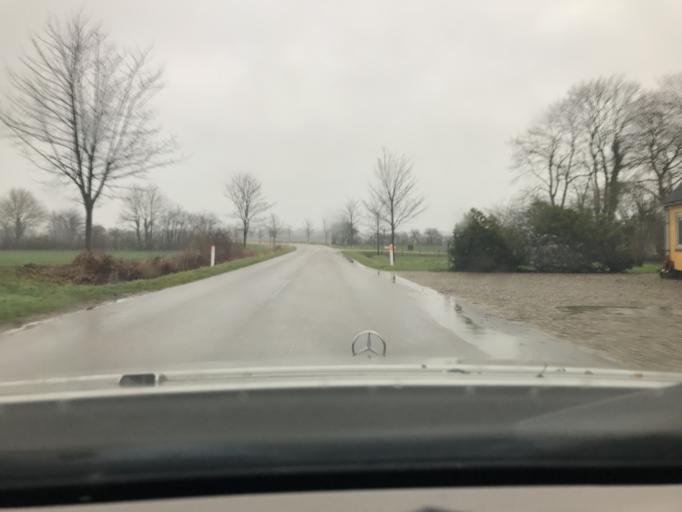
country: DK
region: South Denmark
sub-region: Sonderborg Kommune
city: Horuphav
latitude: 54.8896
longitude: 10.0134
